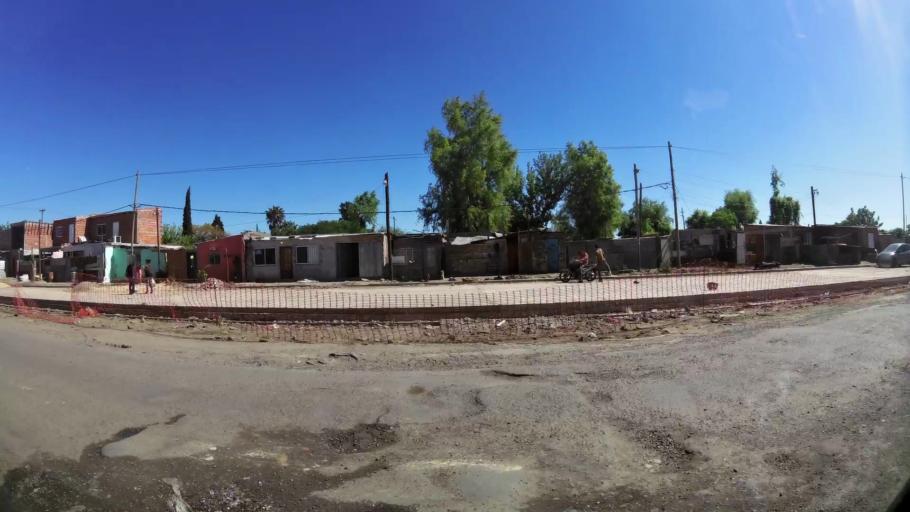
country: AR
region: Santa Fe
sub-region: Departamento de Rosario
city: Rosario
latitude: -32.9705
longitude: -60.6919
